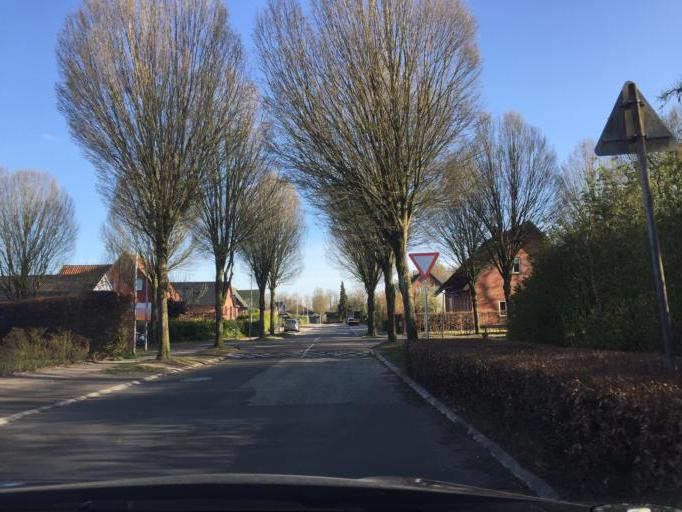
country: DK
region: South Denmark
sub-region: Odense Kommune
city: Odense
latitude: 55.3677
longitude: 10.3673
